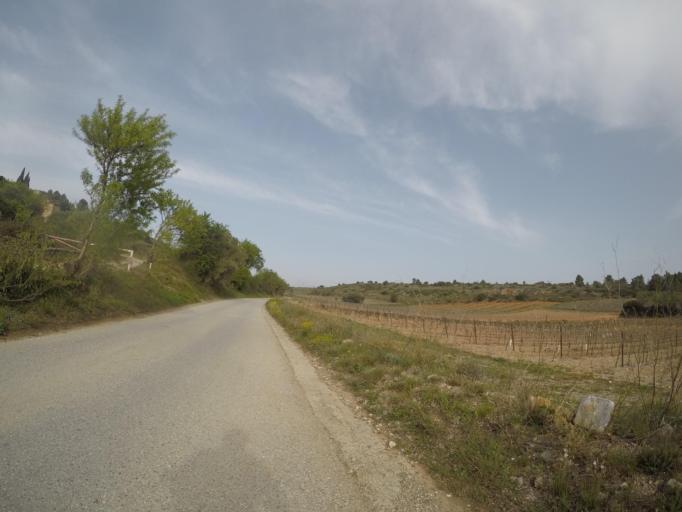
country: FR
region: Languedoc-Roussillon
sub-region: Departement des Pyrenees-Orientales
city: Baixas
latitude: 42.7655
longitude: 2.8152
